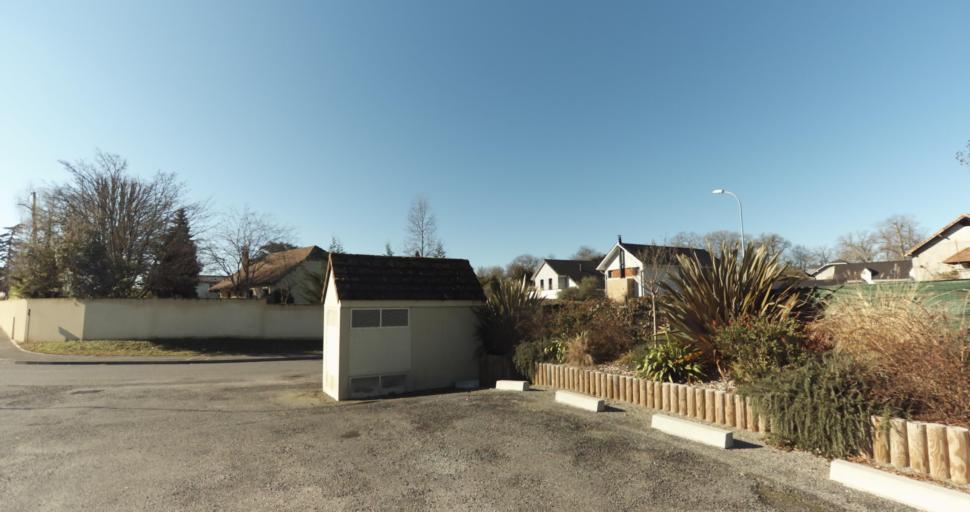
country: FR
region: Aquitaine
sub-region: Departement des Pyrenees-Atlantiques
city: Morlaas
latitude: 43.3495
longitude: -0.2569
